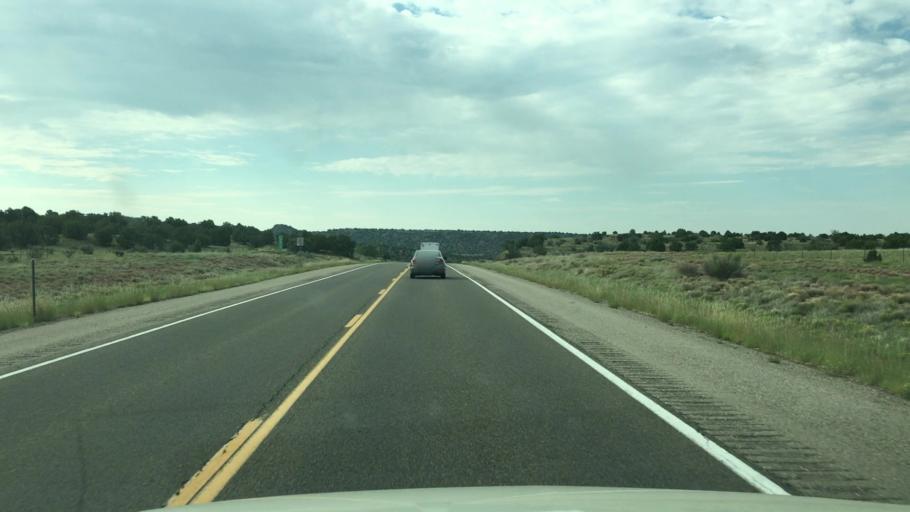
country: US
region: New Mexico
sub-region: Santa Fe County
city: Eldorado at Santa Fe
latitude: 35.2901
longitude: -105.8242
